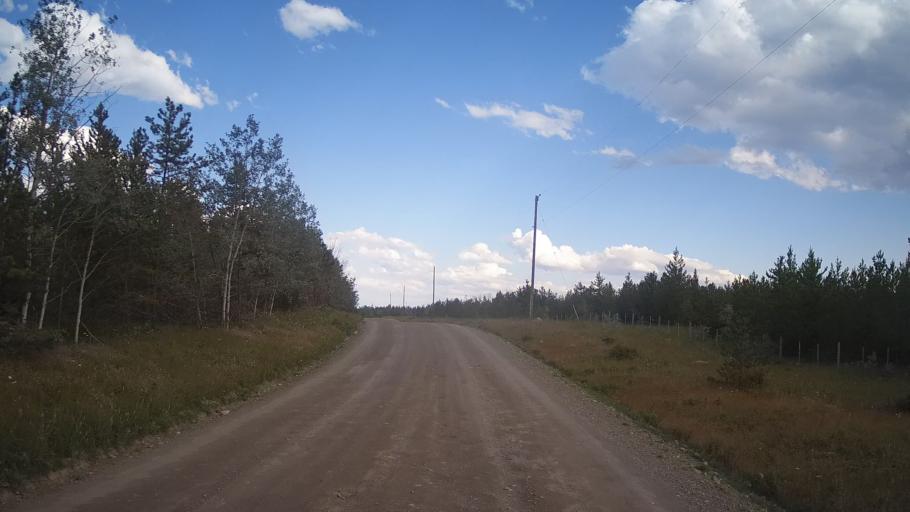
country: CA
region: British Columbia
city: Cache Creek
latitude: 51.2684
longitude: -121.7076
